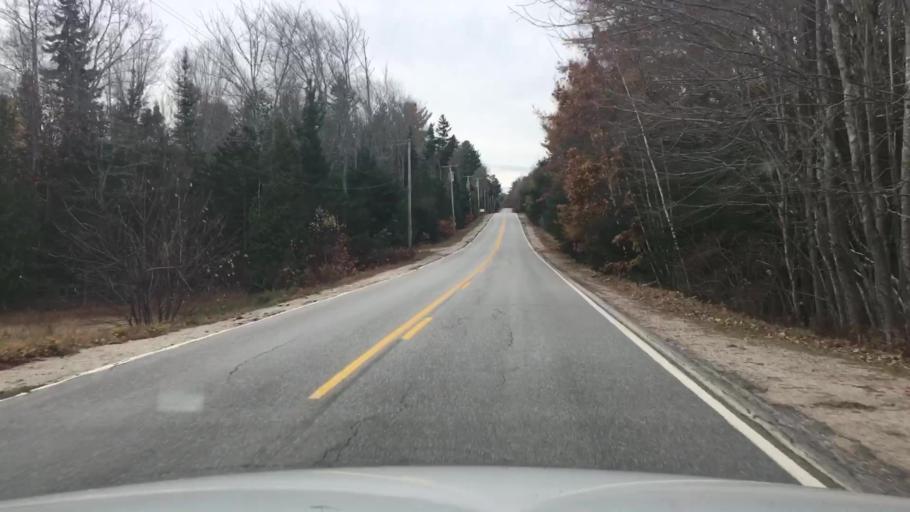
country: US
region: Maine
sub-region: Hancock County
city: Sedgwick
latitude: 44.3149
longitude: -68.5706
